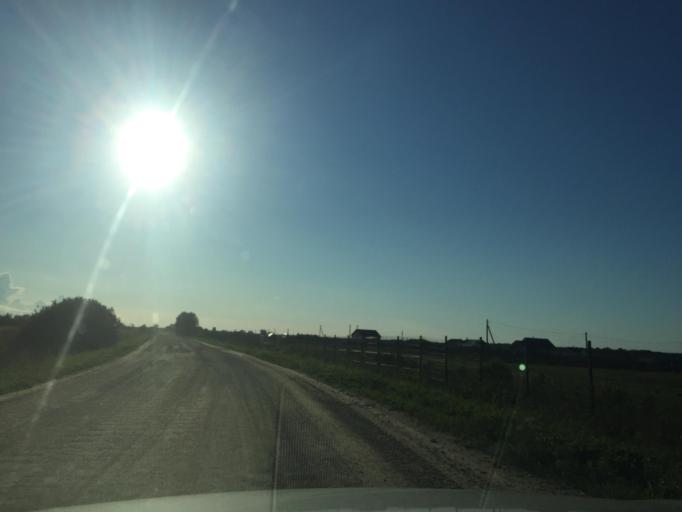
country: RU
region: Leningrad
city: Rozhdestveno
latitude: 59.3325
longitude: 30.0114
